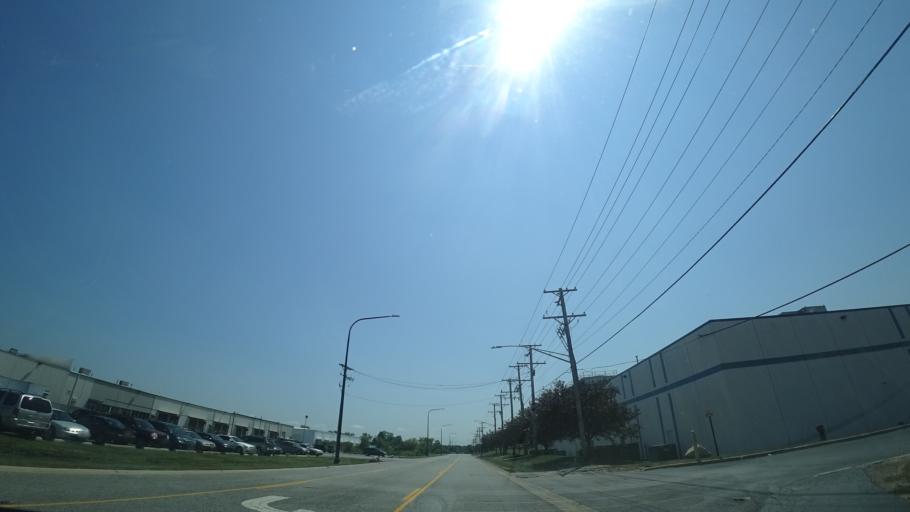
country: US
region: Illinois
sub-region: Cook County
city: Crestwood
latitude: 41.6800
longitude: -87.7590
